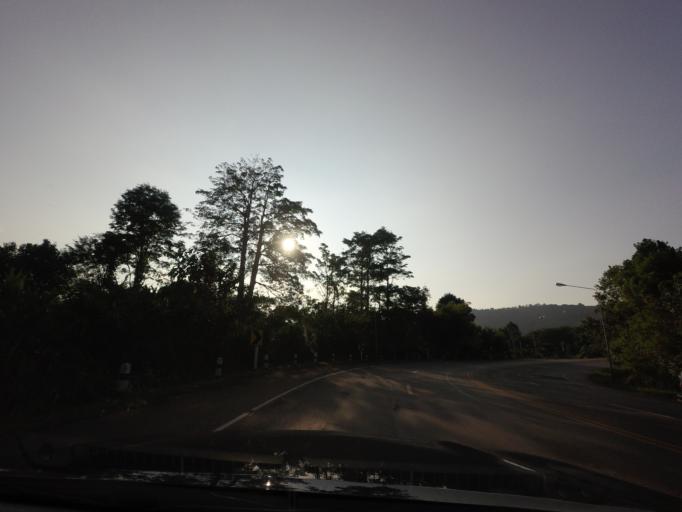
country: TH
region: Loei
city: Dan Sai
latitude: 17.2104
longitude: 101.1536
